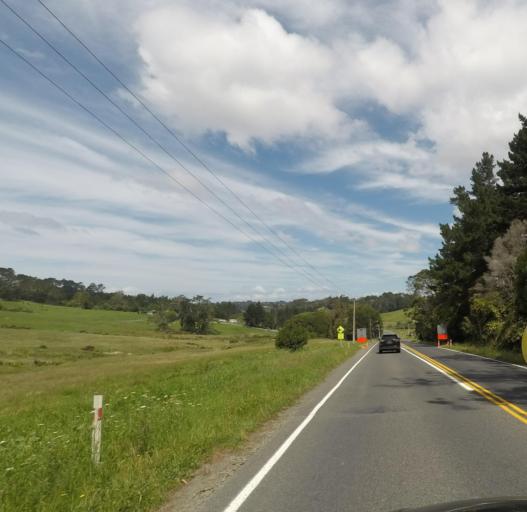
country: NZ
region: Auckland
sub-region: Auckland
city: Rothesay Bay
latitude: -36.6734
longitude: 174.6855
